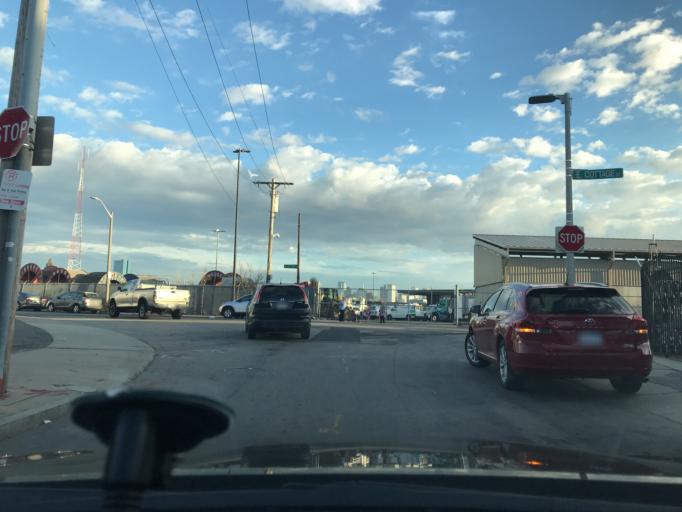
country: US
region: Massachusetts
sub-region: Suffolk County
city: South Boston
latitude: 42.3209
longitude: -71.0654
